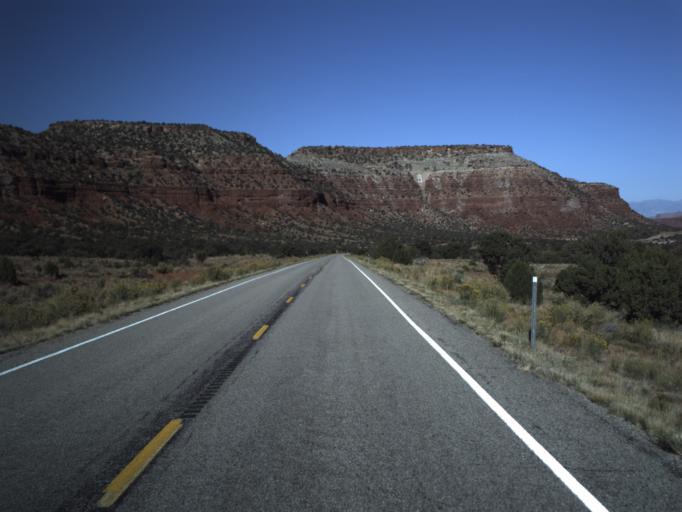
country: US
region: Utah
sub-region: San Juan County
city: Blanding
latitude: 37.6331
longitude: -110.0954
